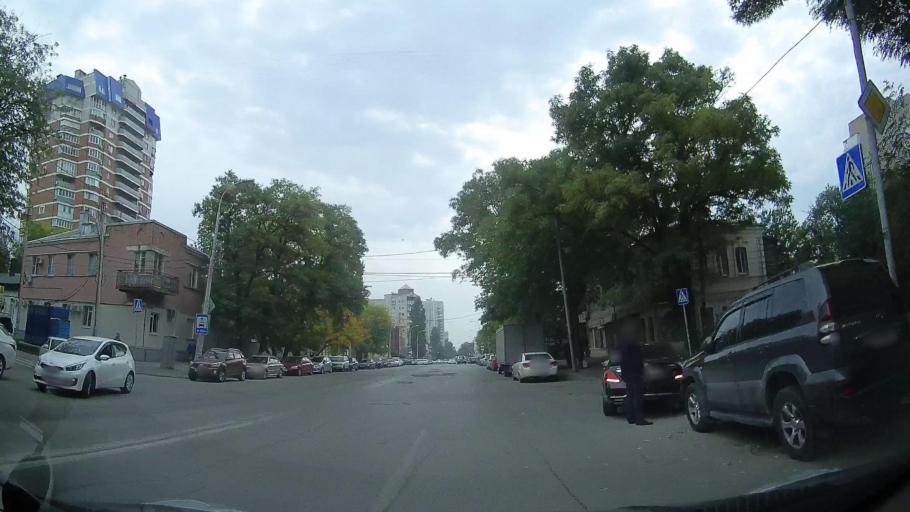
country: RU
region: Rostov
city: Rostov-na-Donu
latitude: 47.2331
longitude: 39.7270
